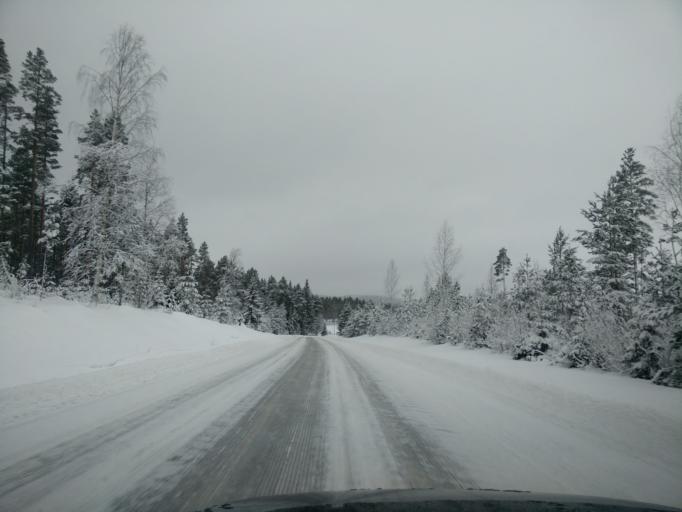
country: SE
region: Vaesternorrland
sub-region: Ange Kommun
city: Ange
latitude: 62.3933
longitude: 15.4039
